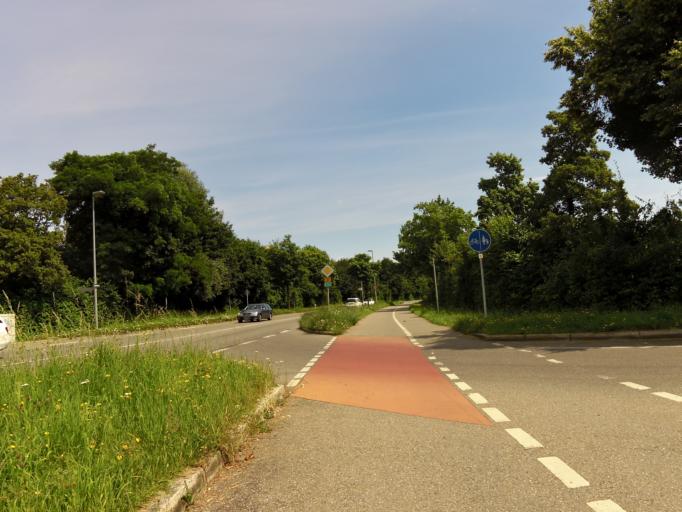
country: DE
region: Baden-Wuerttemberg
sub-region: Tuebingen Region
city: Friedrichshafen
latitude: 47.6639
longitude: 9.4308
